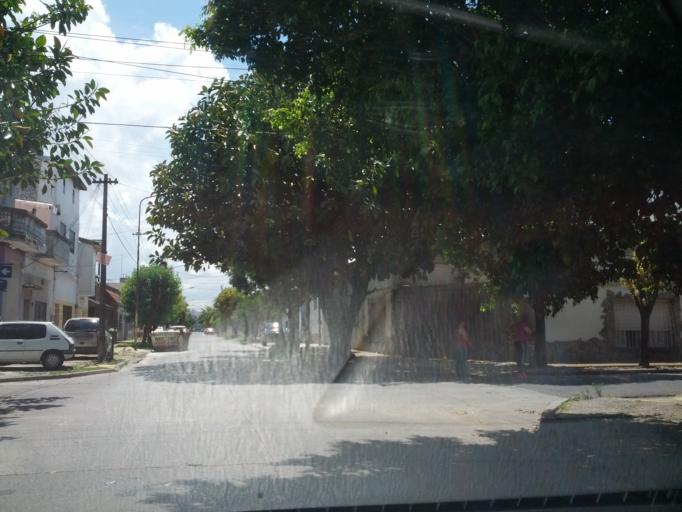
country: AR
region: Buenos Aires
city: San Justo
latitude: -34.6465
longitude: -58.5479
